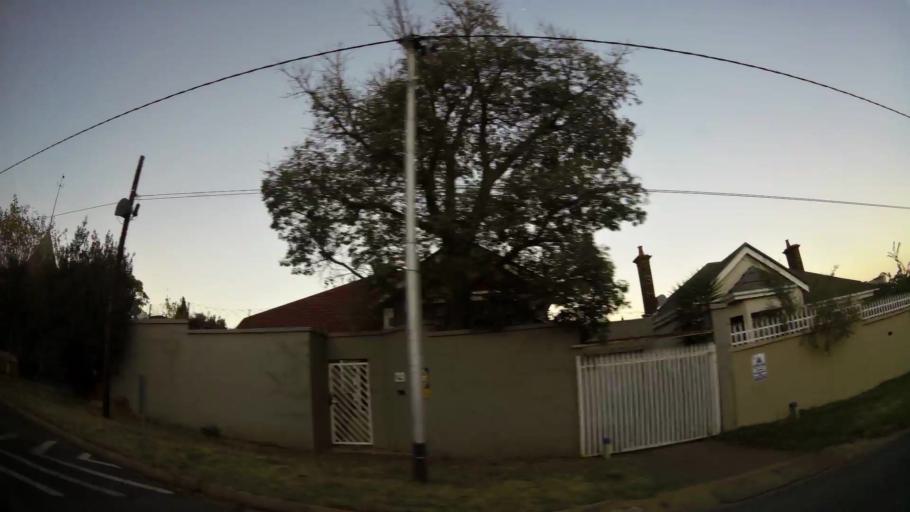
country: ZA
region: Gauteng
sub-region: City of Johannesburg Metropolitan Municipality
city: Roodepoort
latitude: -26.1748
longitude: 27.9179
